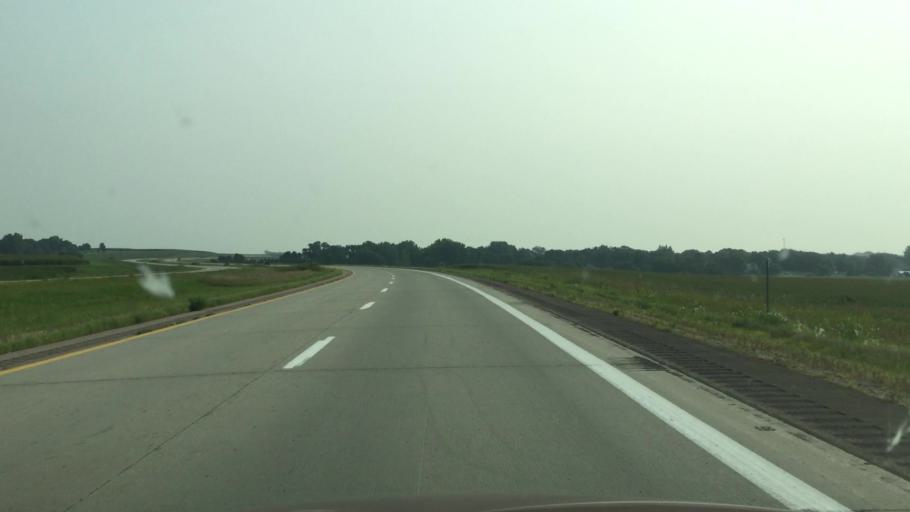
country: US
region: Iowa
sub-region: Plymouth County
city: Le Mars
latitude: 42.8484
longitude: -96.1397
